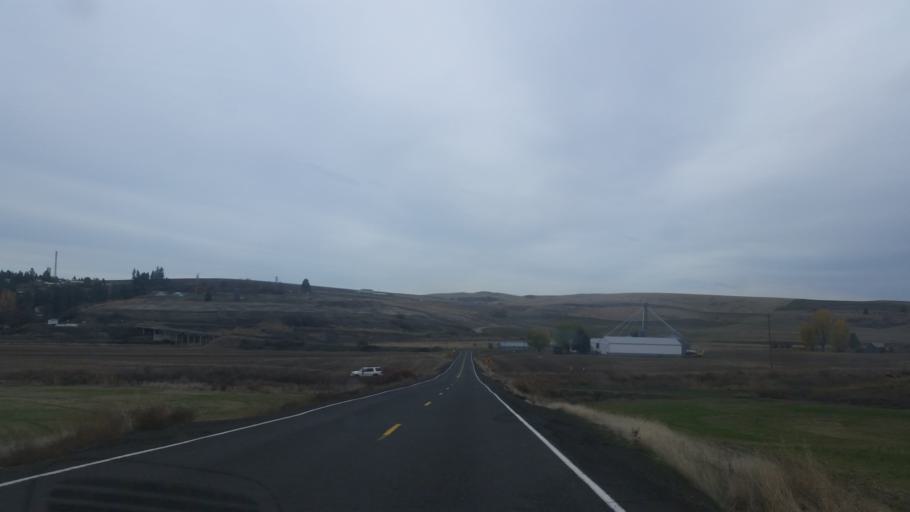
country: US
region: Washington
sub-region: Spokane County
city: Cheney
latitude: 47.2223
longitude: -117.3728
